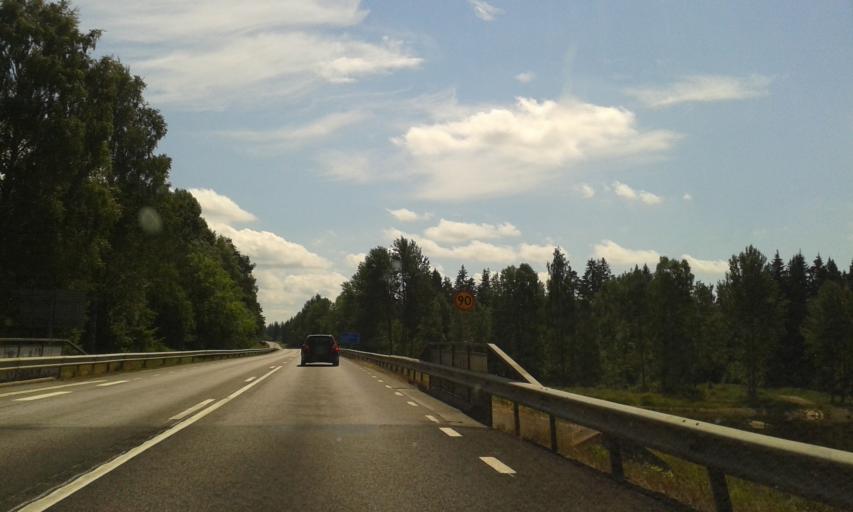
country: SE
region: Joenkoeping
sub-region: Varnamo Kommun
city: Rydaholm
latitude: 56.9841
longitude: 14.3015
